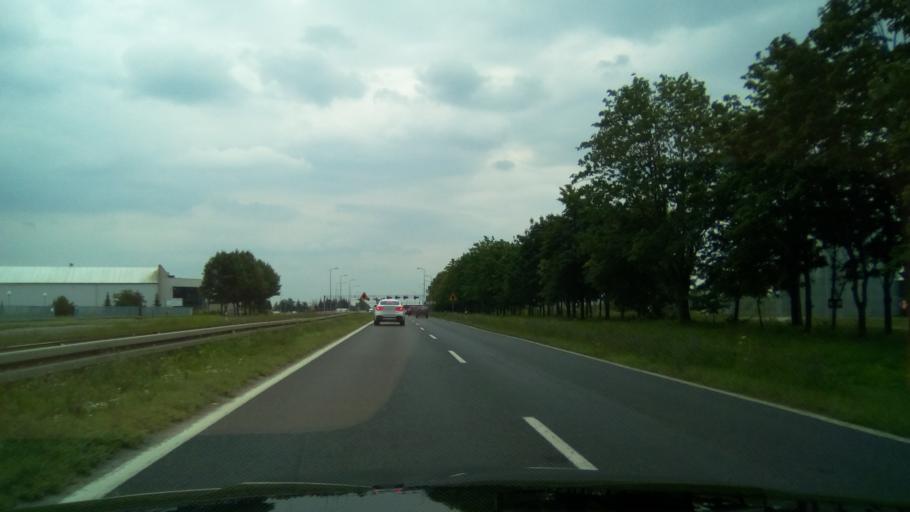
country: PL
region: Greater Poland Voivodeship
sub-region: Powiat poznanski
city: Swarzedz
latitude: 52.4034
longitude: 17.1185
